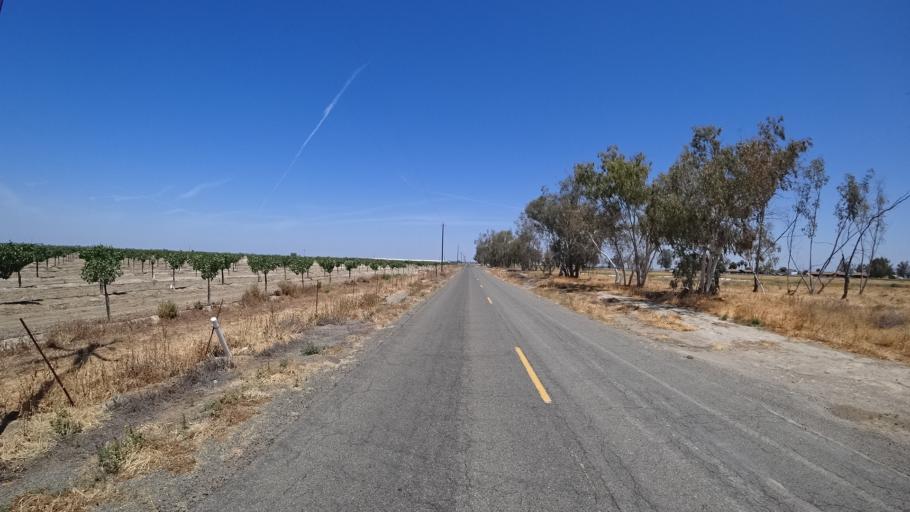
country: US
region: California
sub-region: Kings County
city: Armona
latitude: 36.2077
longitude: -119.7086
